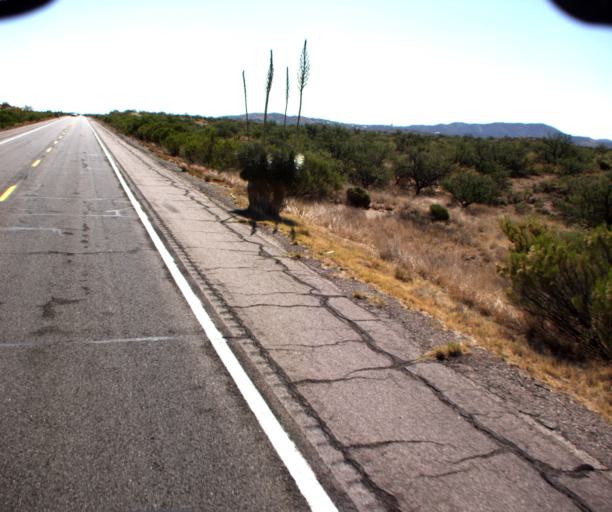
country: US
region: Arizona
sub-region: Pinal County
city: Oracle
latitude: 32.6124
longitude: -110.8391
